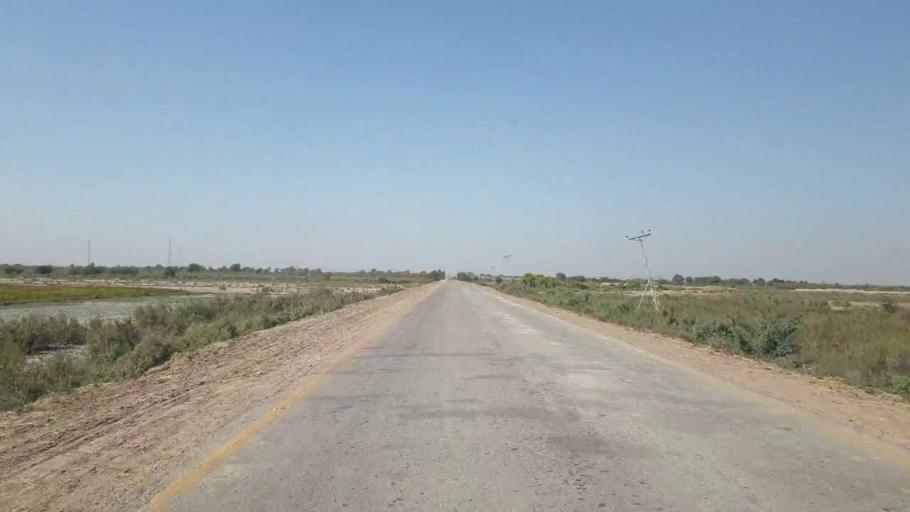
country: PK
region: Sindh
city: Rajo Khanani
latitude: 25.0549
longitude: 68.8050
